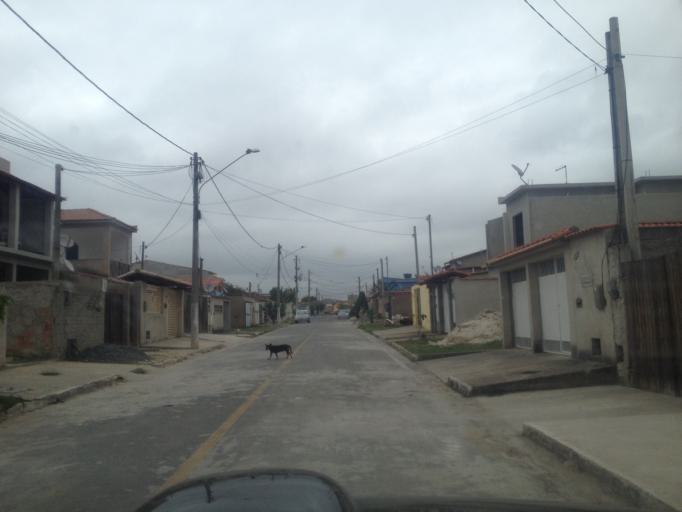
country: BR
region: Rio de Janeiro
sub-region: Porto Real
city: Porto Real
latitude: -22.4116
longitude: -44.3070
